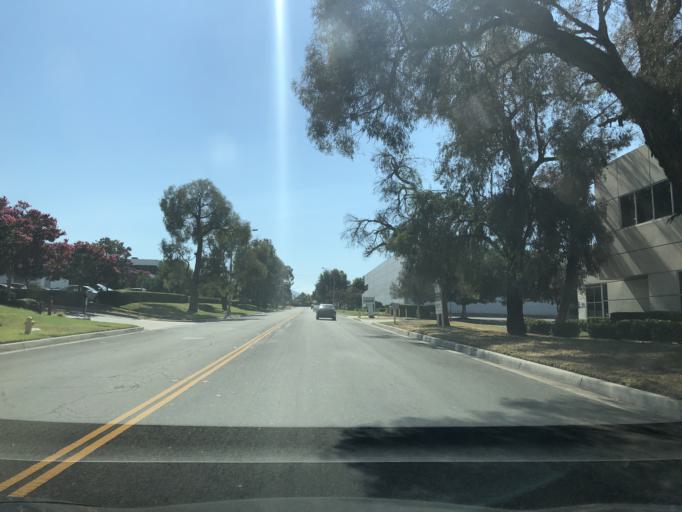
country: US
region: California
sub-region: Riverside County
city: Home Gardens
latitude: 33.8616
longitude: -117.5410
